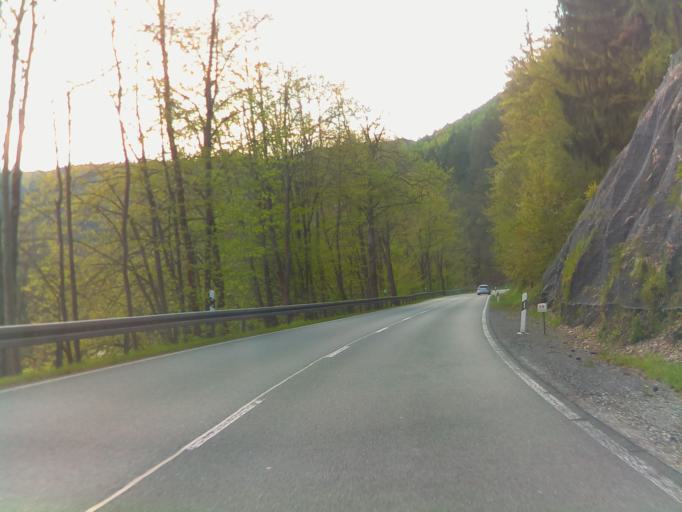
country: DE
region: Thuringia
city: Probstzella
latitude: 50.5456
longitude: 11.3626
